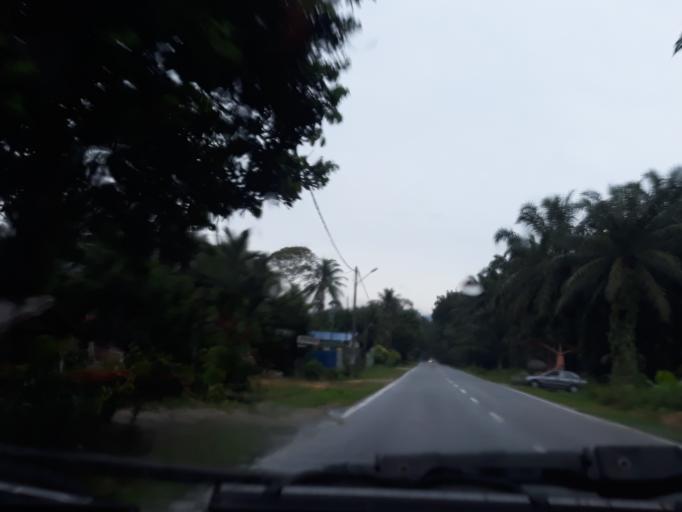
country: MY
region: Kedah
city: Kulim
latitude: 5.2294
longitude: 100.6057
